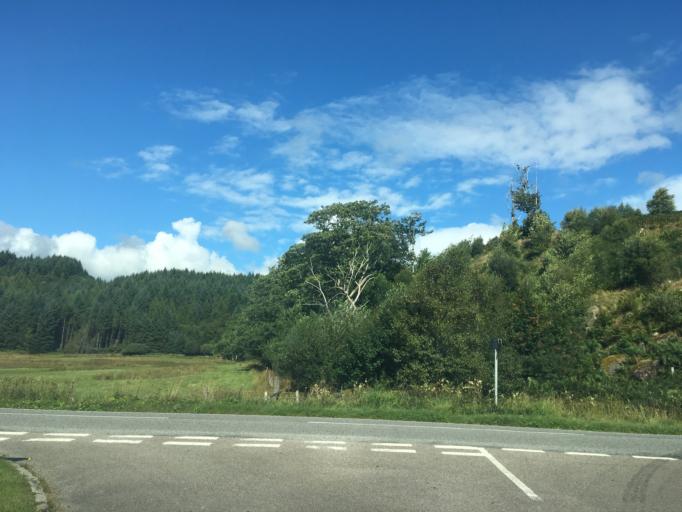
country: GB
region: Scotland
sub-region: Argyll and Bute
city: Lochgilphead
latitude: 56.0883
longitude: -5.4684
